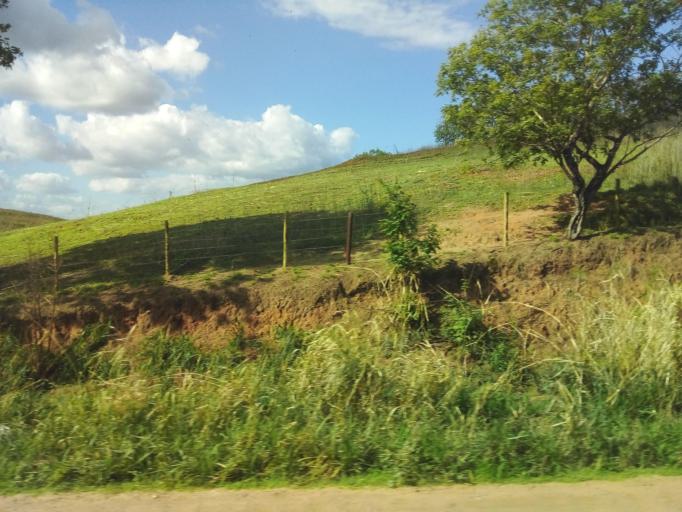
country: BR
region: Minas Gerais
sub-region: Conselheiro Pena
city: Conselheiro Pena
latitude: -18.9824
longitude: -41.6153
